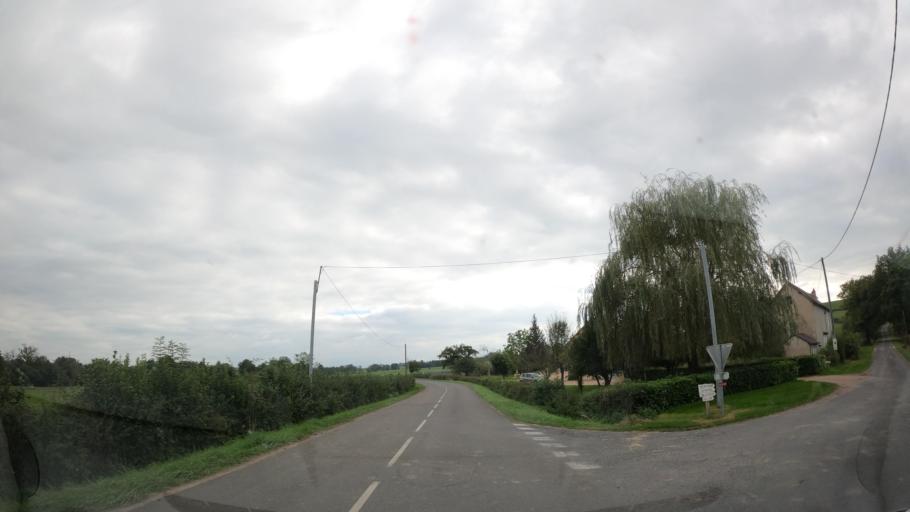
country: FR
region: Auvergne
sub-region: Departement de l'Allier
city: Lapalisse
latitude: 46.3229
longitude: 3.6310
